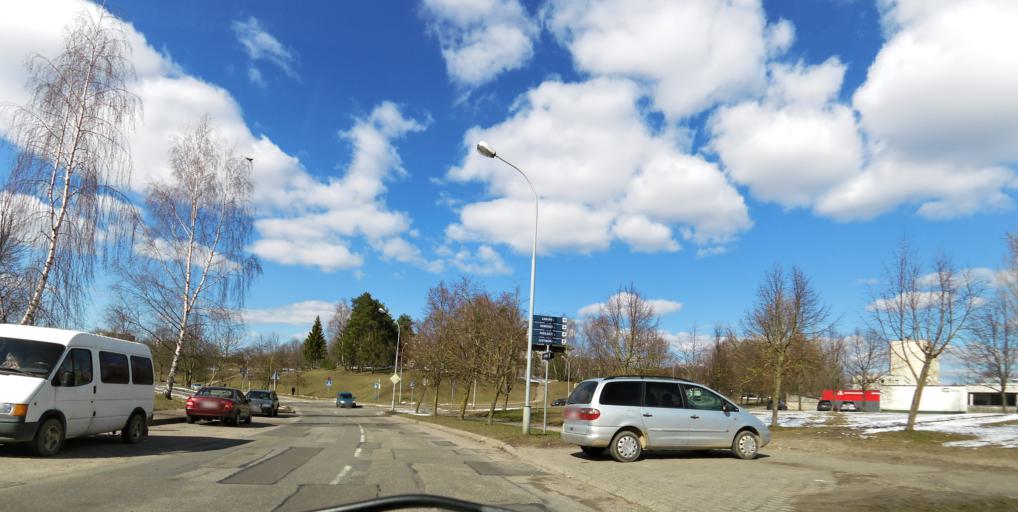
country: LT
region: Vilnius County
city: Pasilaiciai
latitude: 54.7289
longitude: 25.2261
